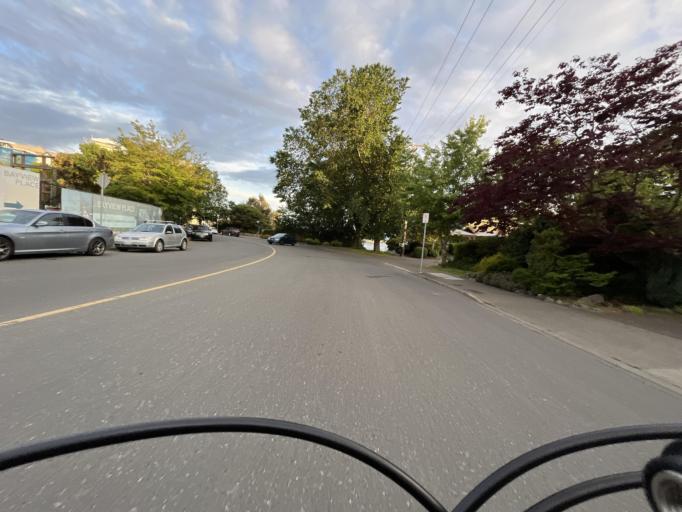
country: CA
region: British Columbia
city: Victoria
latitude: 48.4297
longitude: -123.3848
